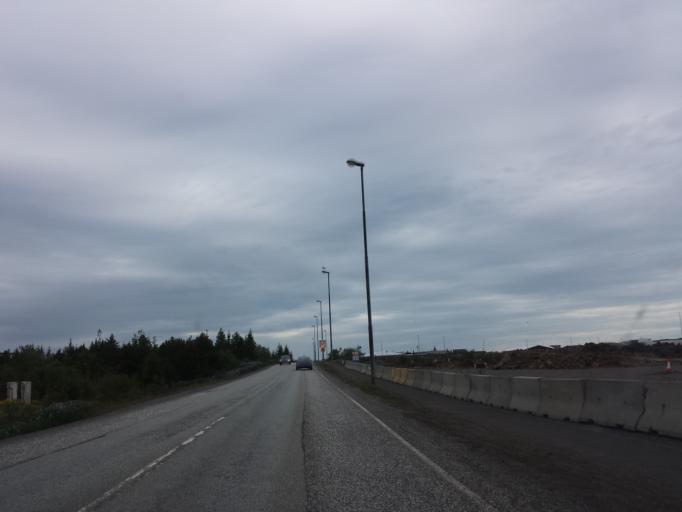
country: IS
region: Capital Region
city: Hafnarfjoerdur
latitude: 64.0849
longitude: -21.9529
